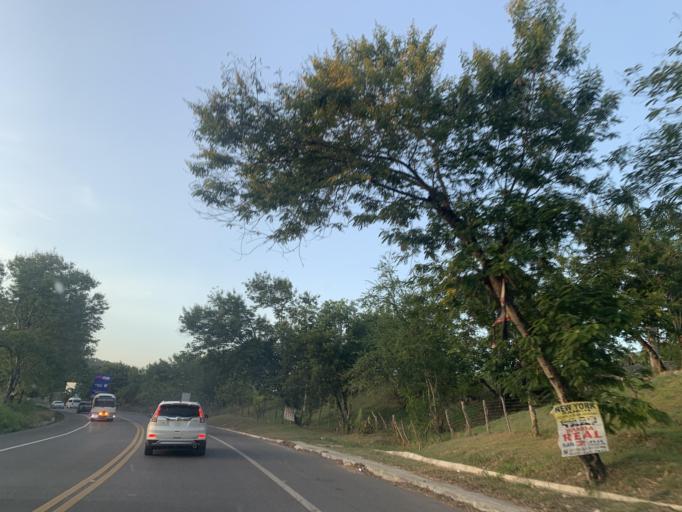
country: DO
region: Puerto Plata
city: Imbert
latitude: 19.7622
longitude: -70.8330
